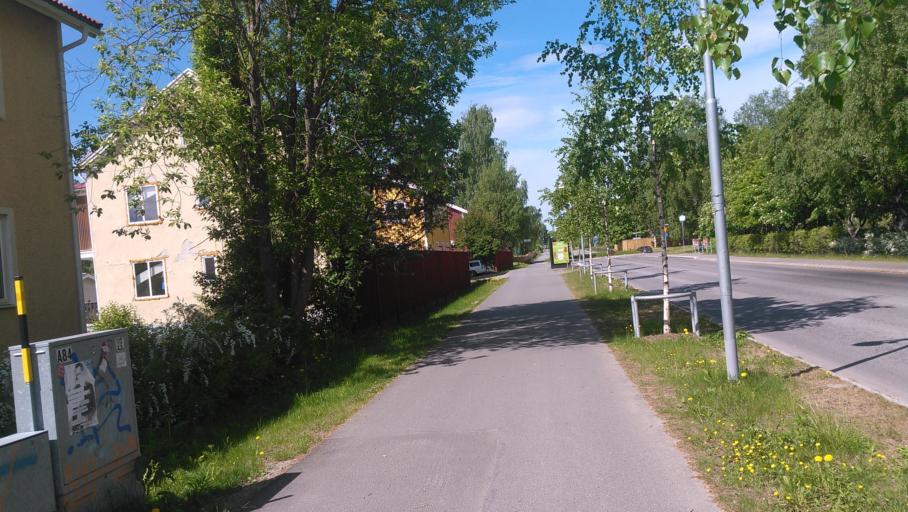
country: SE
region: Vaesterbotten
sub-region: Umea Kommun
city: Roback
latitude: 63.8349
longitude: 20.2001
